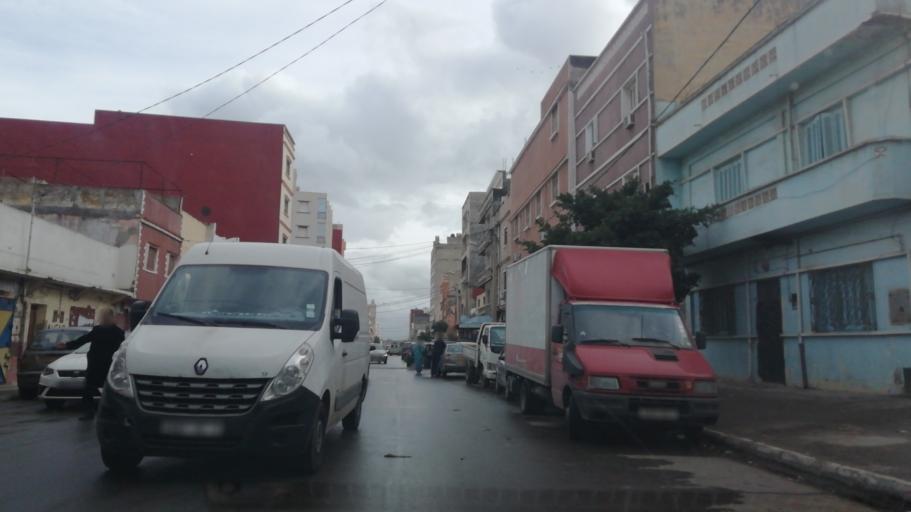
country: DZ
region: Oran
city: Oran
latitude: 35.6870
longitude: -0.6440
